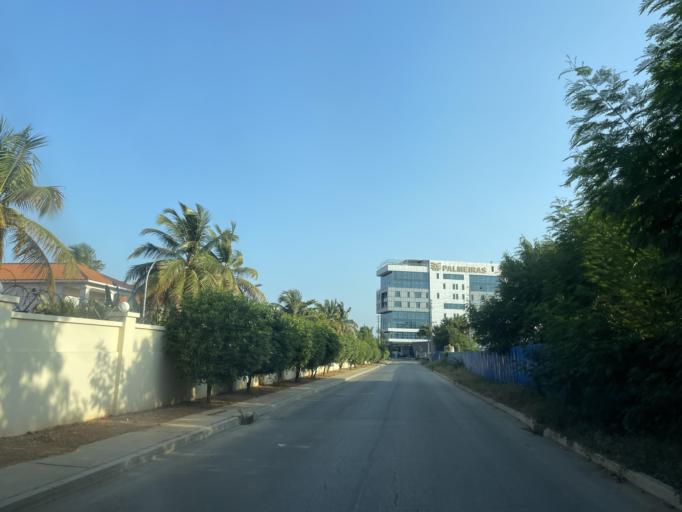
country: AO
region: Luanda
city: Luanda
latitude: -8.9102
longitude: 13.1889
